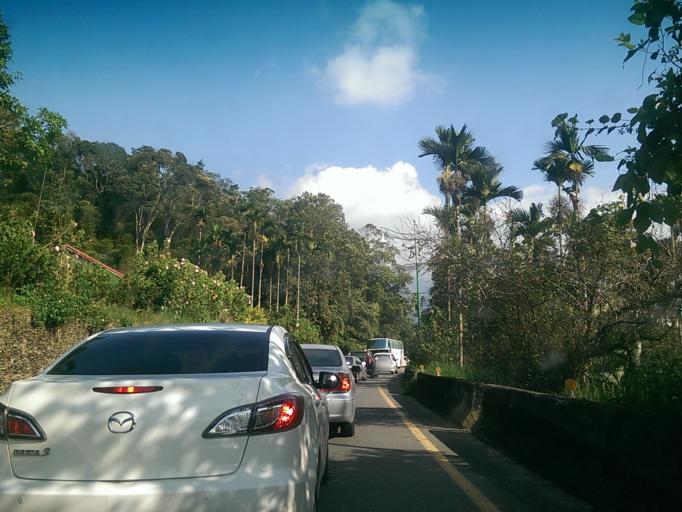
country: TW
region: Taiwan
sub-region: Nantou
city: Puli
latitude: 23.8675
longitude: 120.9034
